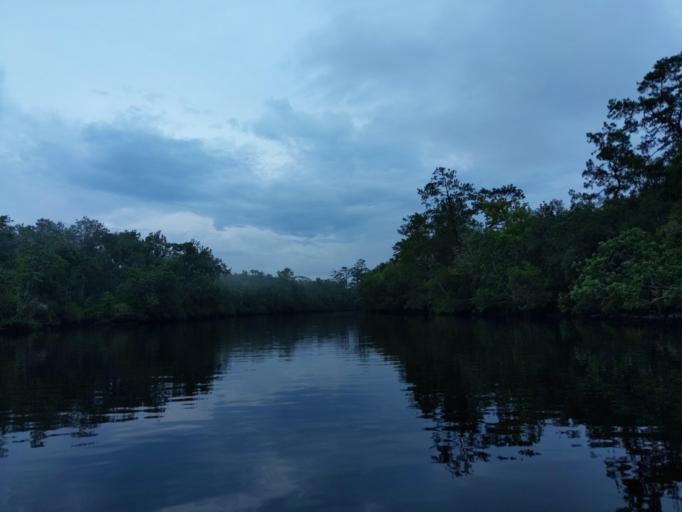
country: US
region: Florida
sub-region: Wakulla County
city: Crawfordville
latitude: 30.0334
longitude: -84.5136
